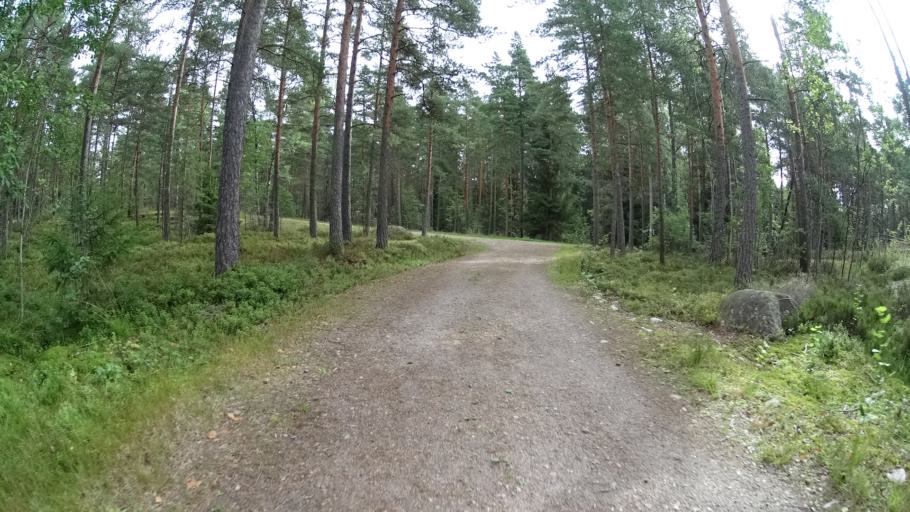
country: FI
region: Uusimaa
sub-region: Helsinki
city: Kilo
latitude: 60.2304
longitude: 24.7896
